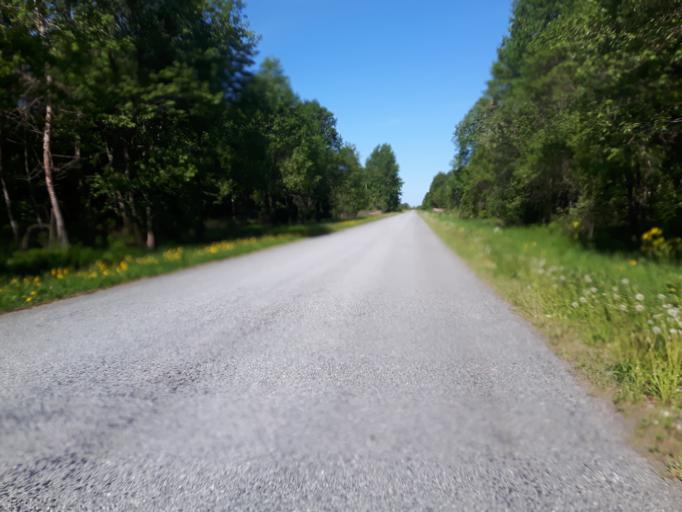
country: EE
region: Ida-Virumaa
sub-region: Aseri vald
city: Aseri
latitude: 59.4569
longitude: 26.8424
